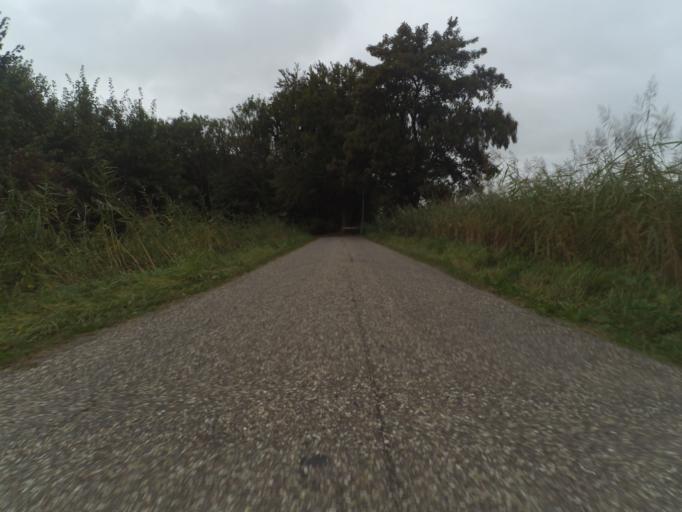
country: NL
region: Gelderland
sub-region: Gemeente Tiel
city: Tiel
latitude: 51.9056
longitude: 5.3983
